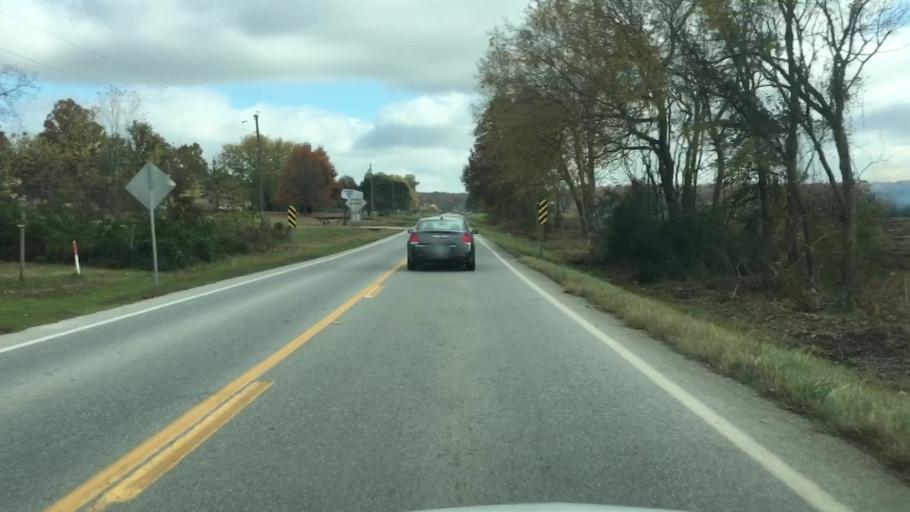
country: US
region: Arkansas
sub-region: Benton County
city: Gentry
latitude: 36.2559
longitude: -94.4474
